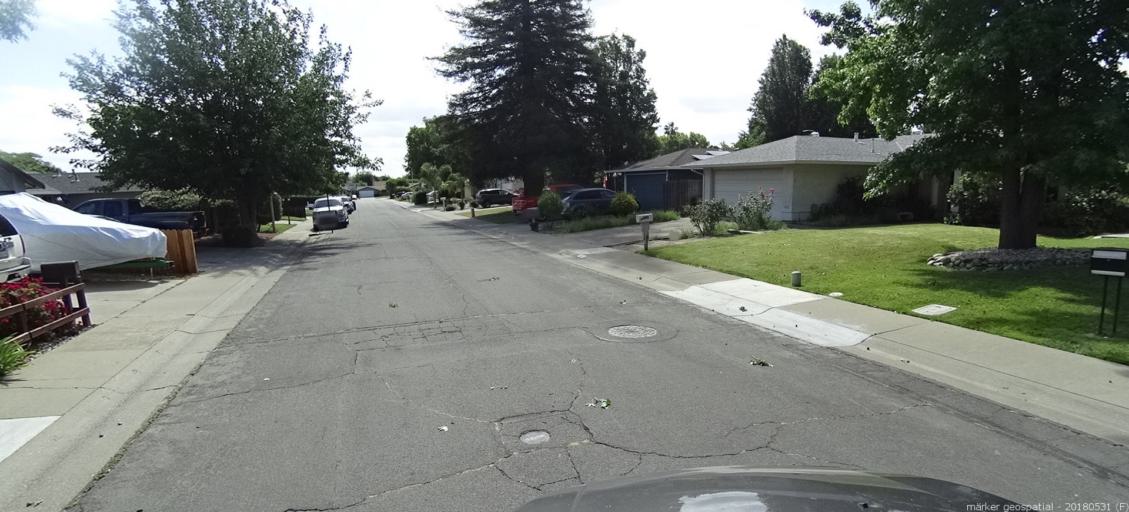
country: US
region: California
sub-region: Sacramento County
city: Sacramento
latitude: 38.6200
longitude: -121.5051
